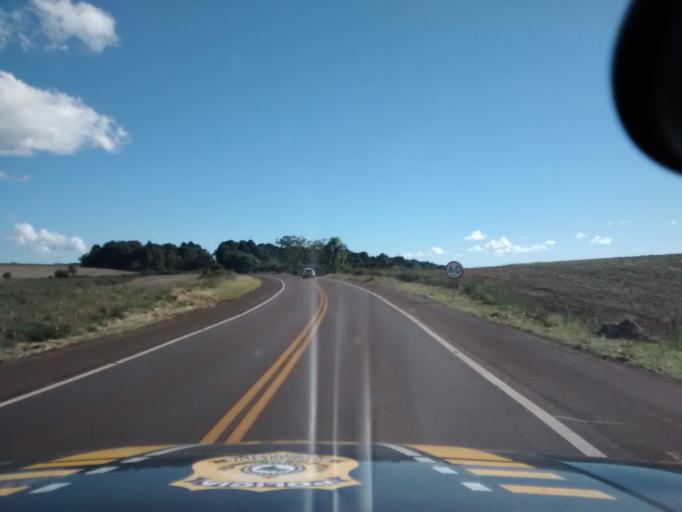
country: BR
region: Rio Grande do Sul
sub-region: Lagoa Vermelha
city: Lagoa Vermelha
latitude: -28.3269
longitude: -51.2709
